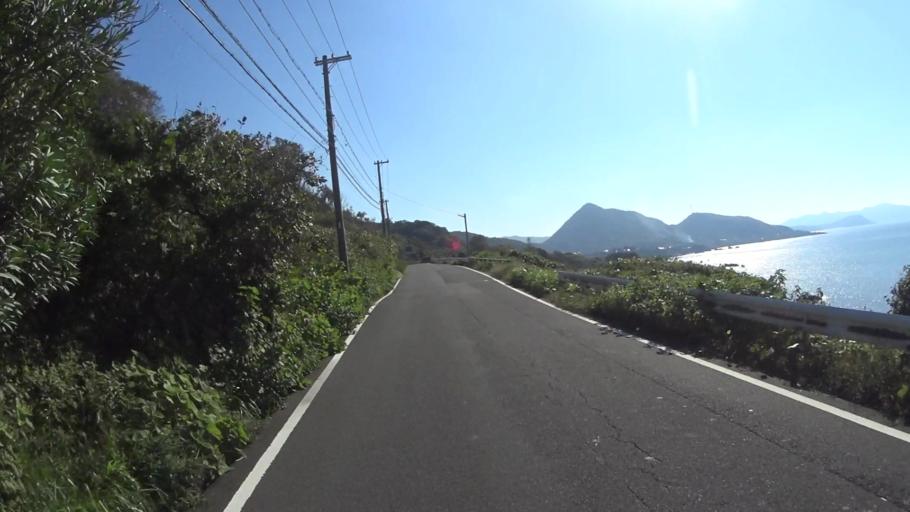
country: JP
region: Kyoto
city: Miyazu
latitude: 35.7325
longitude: 135.0887
